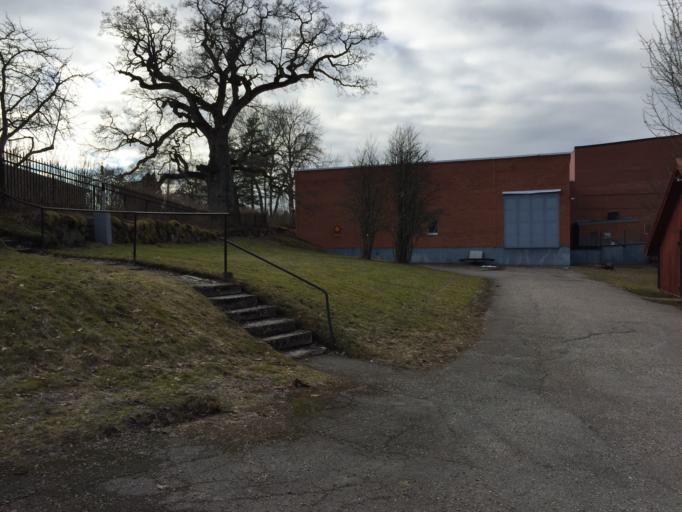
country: SE
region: Soedermanland
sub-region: Vingakers Kommun
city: Vingaker
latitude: 59.0241
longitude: 15.6753
